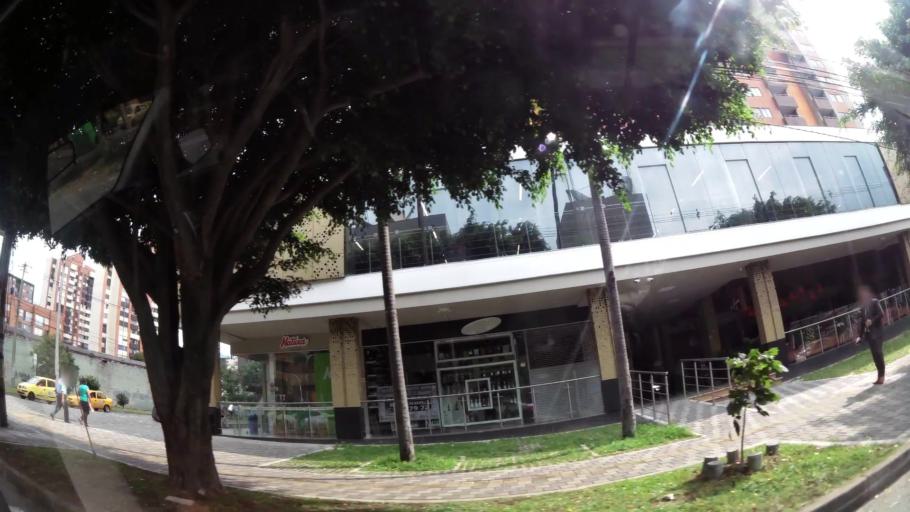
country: CO
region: Antioquia
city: Medellin
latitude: 6.2611
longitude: -75.5868
